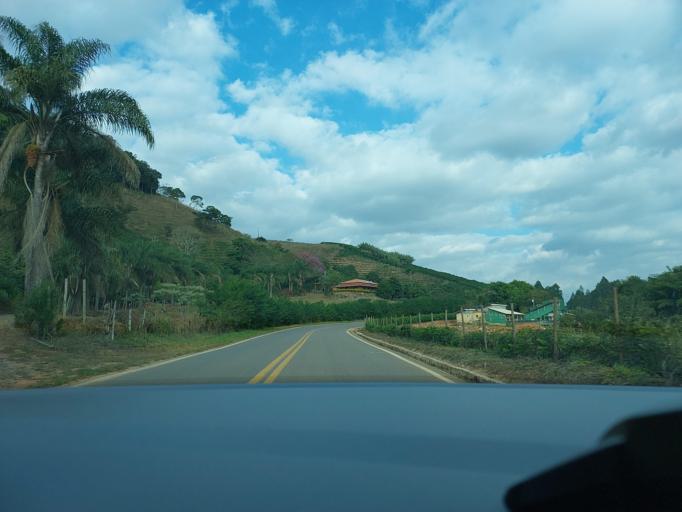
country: BR
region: Minas Gerais
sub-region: Visconde Do Rio Branco
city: Visconde do Rio Branco
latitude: -20.8863
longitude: -42.6596
